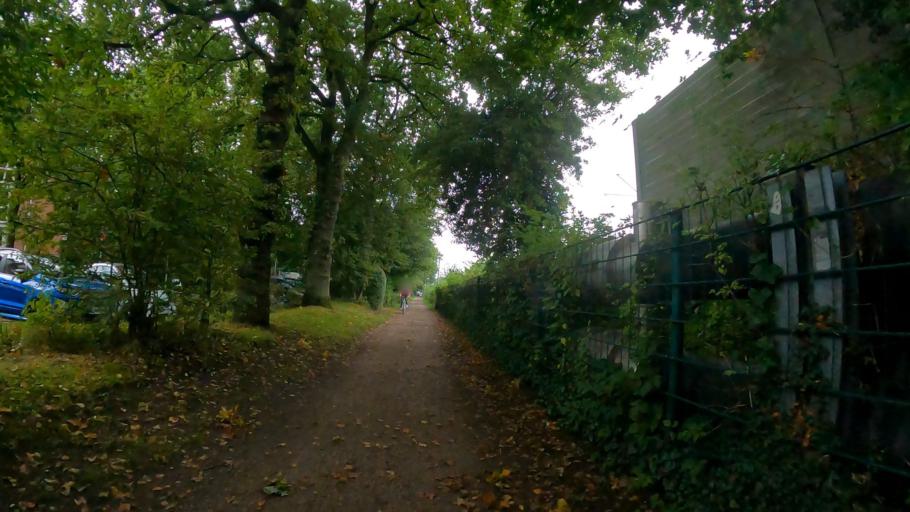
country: DE
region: Schleswig-Holstein
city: Rellingen
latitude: 53.6472
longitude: 9.8090
